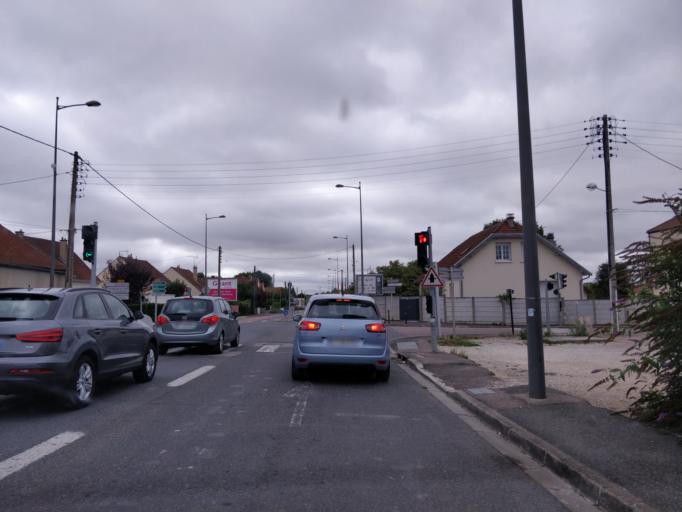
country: FR
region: Champagne-Ardenne
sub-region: Departement de l'Aube
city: Saint-Andre-les-Vergers
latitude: 48.2744
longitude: 4.0587
